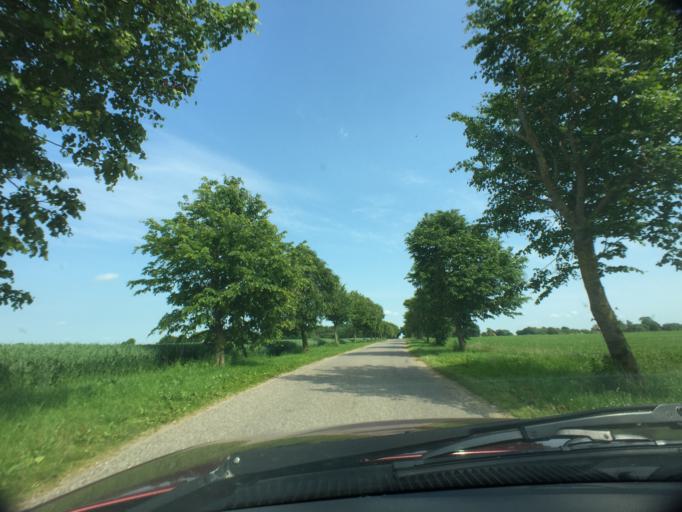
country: DK
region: Central Jutland
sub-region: Viborg Kommune
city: Bjerringbro
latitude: 56.2530
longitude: 9.7159
